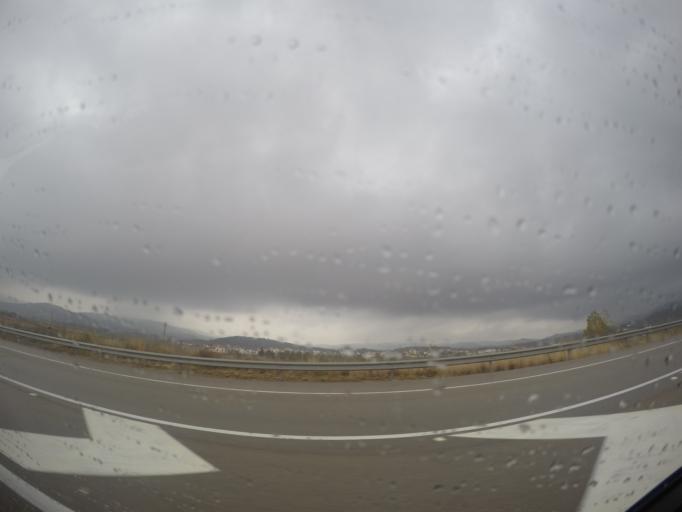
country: ES
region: Catalonia
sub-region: Provincia de Tarragona
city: la Bisbal del Penedes
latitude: 41.2840
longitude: 1.4979
